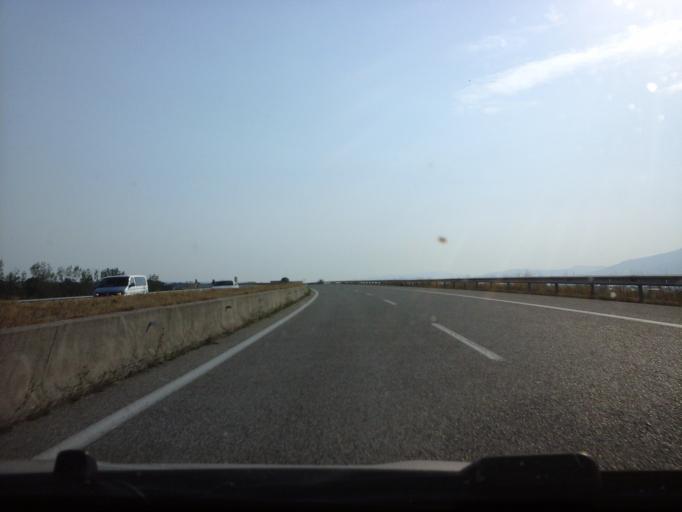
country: GR
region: East Macedonia and Thrace
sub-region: Nomos Xanthis
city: Selero
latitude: 41.1182
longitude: 24.9870
